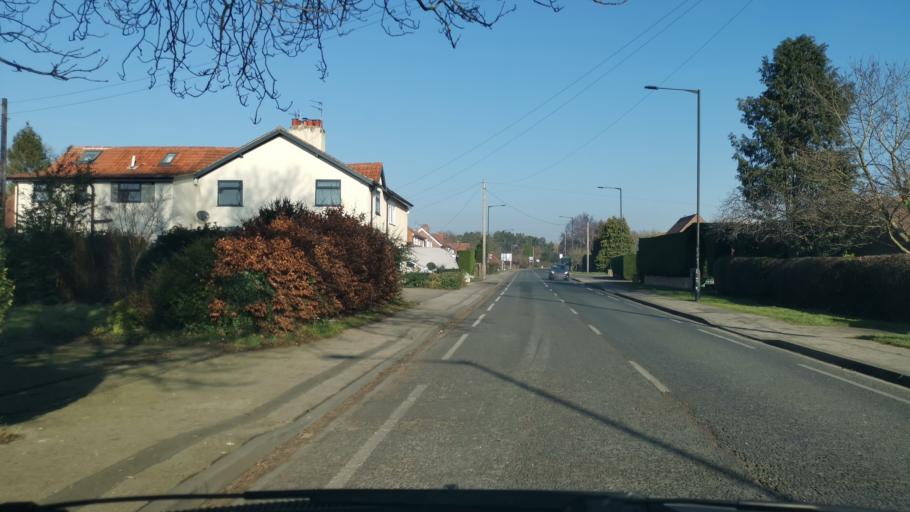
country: GB
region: England
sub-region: City of York
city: Huntington
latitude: 54.0021
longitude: -1.0576
